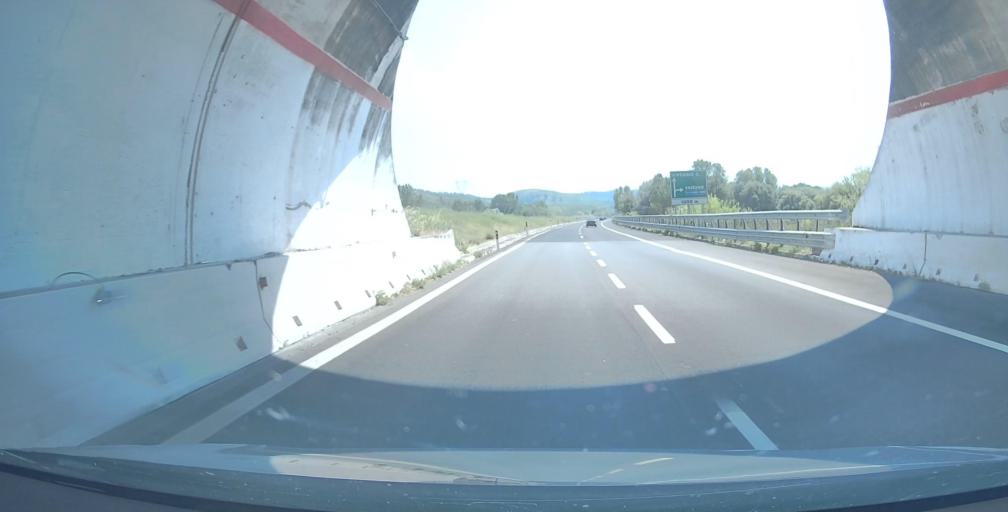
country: IT
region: Calabria
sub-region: Provincia di Vibo-Valentia
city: Filogaso
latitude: 38.6515
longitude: 16.1879
